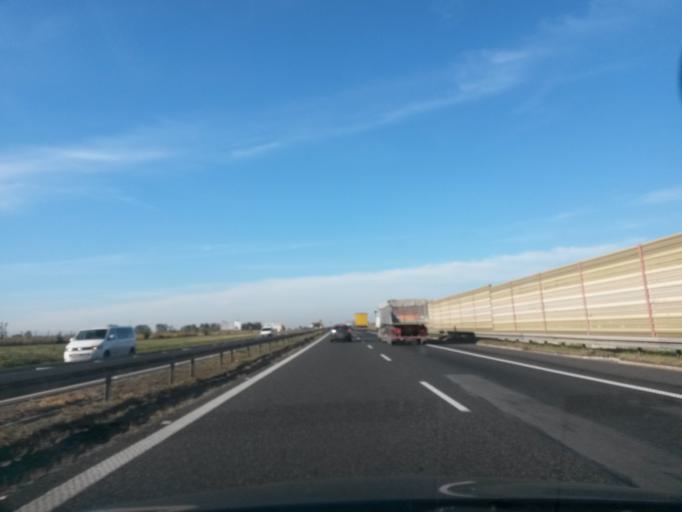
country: PL
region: Lower Silesian Voivodeship
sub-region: Powiat wroclawski
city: Zorawina
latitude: 50.9803
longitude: 17.0604
